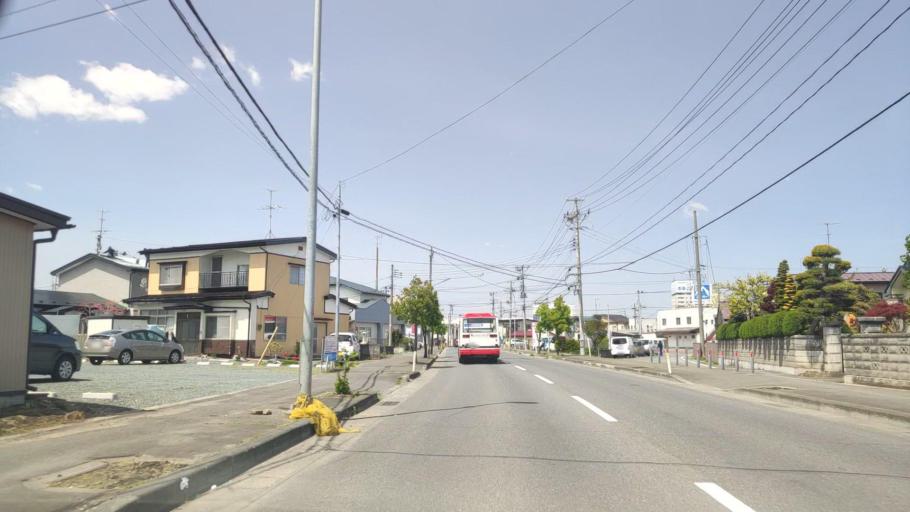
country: JP
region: Aomori
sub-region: Hachinohe Shi
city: Uchimaru
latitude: 40.5063
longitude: 141.4376
